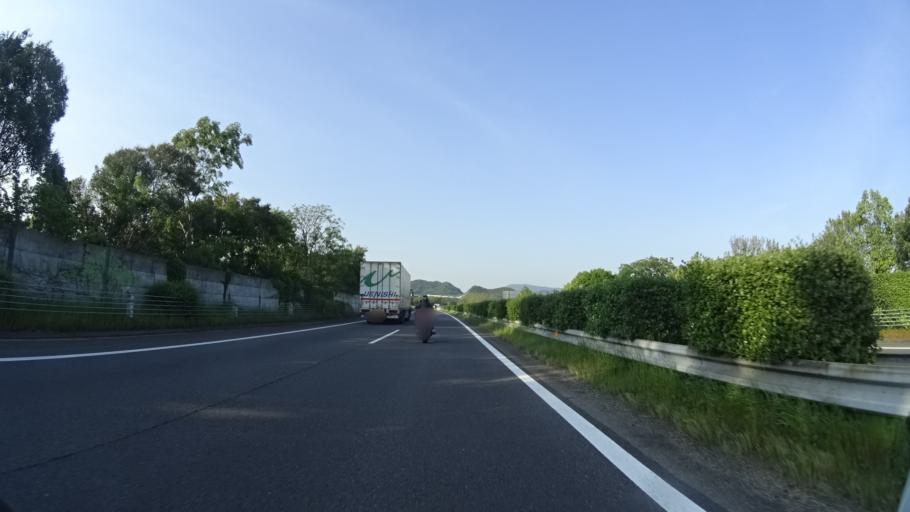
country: JP
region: Kagawa
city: Kan'onjicho
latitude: 34.1337
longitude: 133.7071
